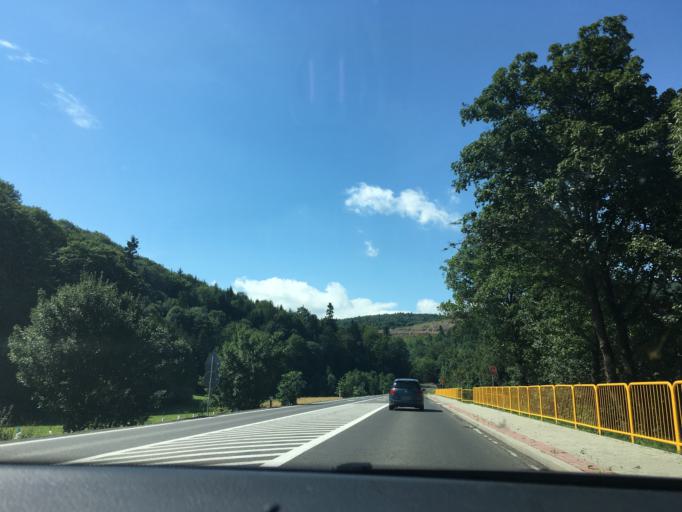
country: PL
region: Subcarpathian Voivodeship
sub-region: Powiat krosnienski
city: Dukla
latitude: 49.5220
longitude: 21.6889
